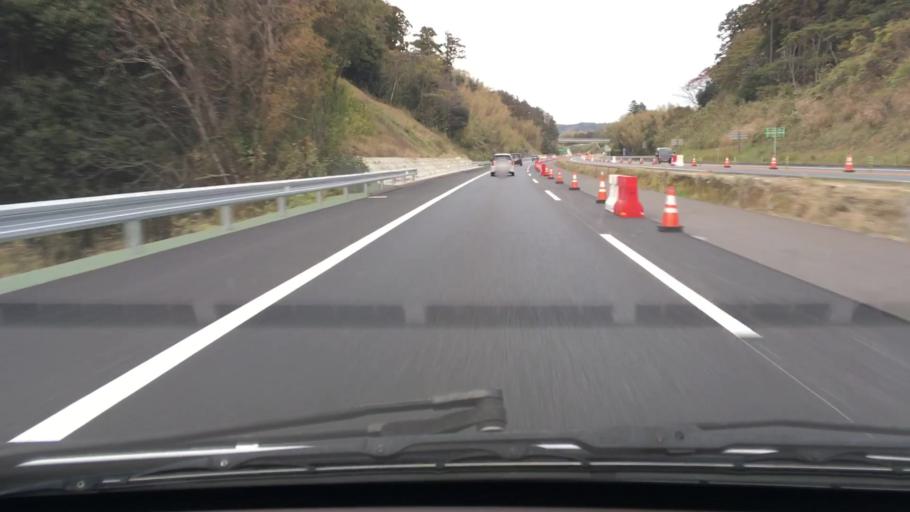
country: JP
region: Chiba
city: Kimitsu
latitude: 35.2953
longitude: 139.9335
